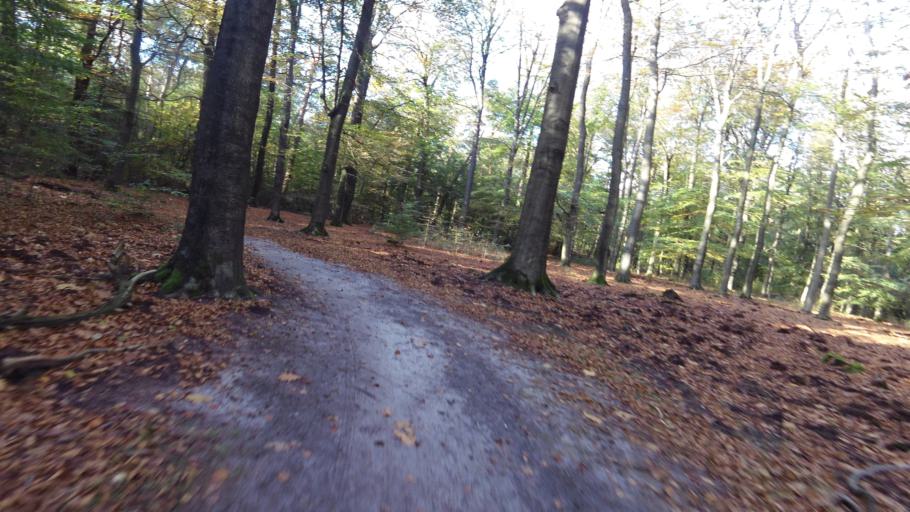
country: NL
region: Gelderland
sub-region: Gemeente Epe
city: Epe
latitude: 52.3918
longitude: 5.9577
